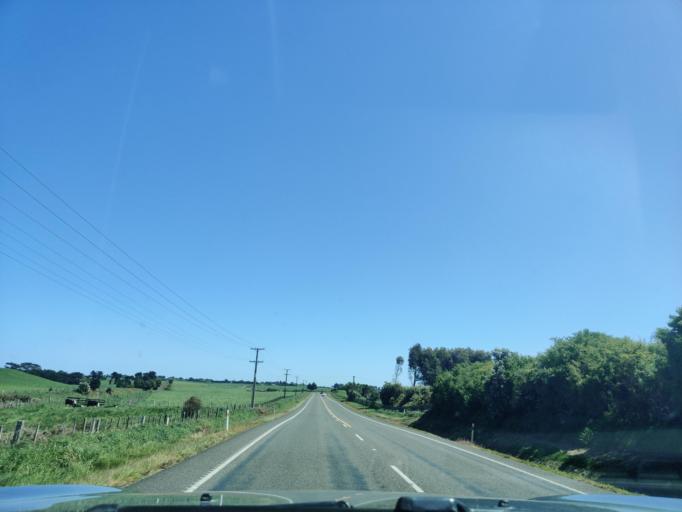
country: NZ
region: Taranaki
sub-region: South Taranaki District
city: Patea
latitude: -39.7728
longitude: 174.6736
